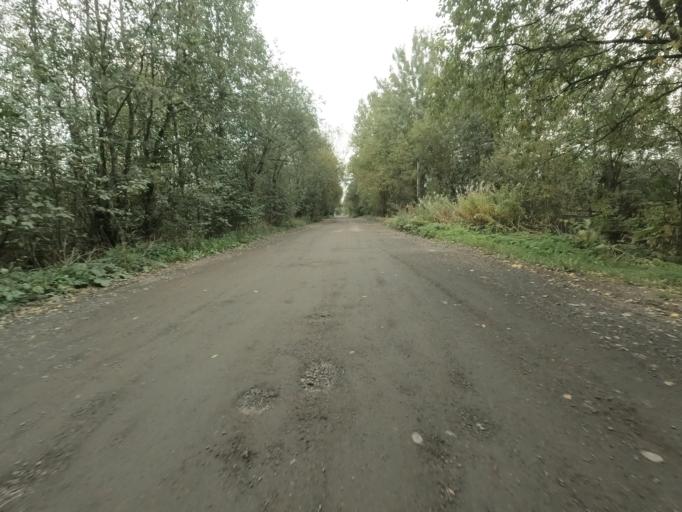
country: RU
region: St.-Petersburg
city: Sapernyy
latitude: 59.7639
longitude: 30.6452
